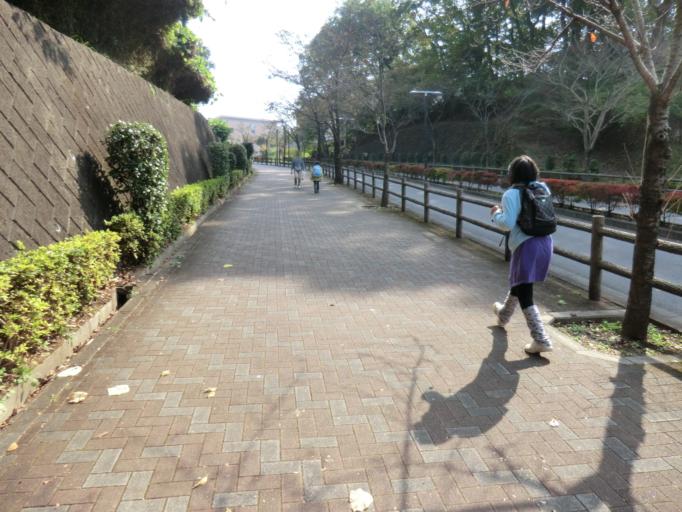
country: JP
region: Tokyo
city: Hino
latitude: 35.6453
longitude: 139.4048
